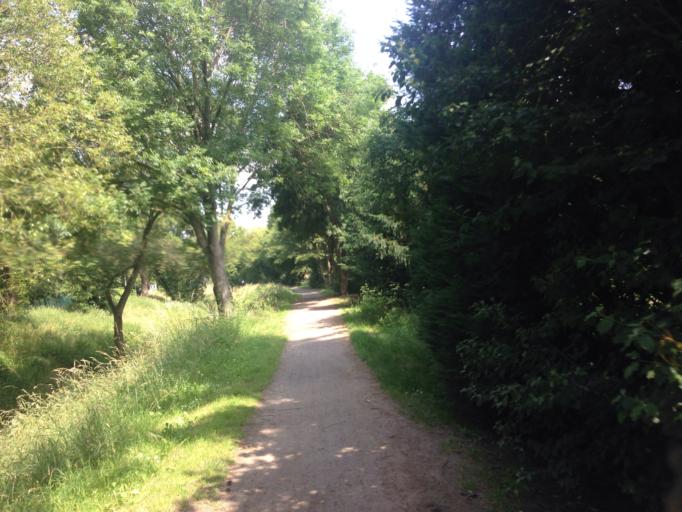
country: DE
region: Hesse
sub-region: Regierungsbezirk Darmstadt
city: Hanau am Main
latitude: 50.1428
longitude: 8.9152
